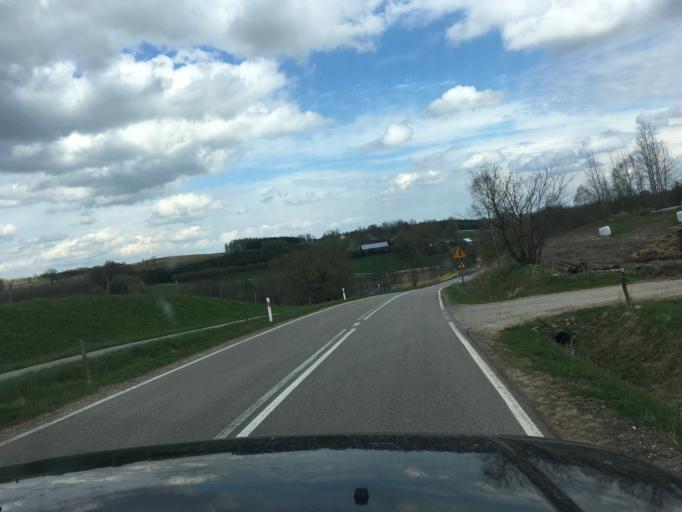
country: PL
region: Podlasie
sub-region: Powiat suwalski
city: Filipow
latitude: 54.3610
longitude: 22.8012
